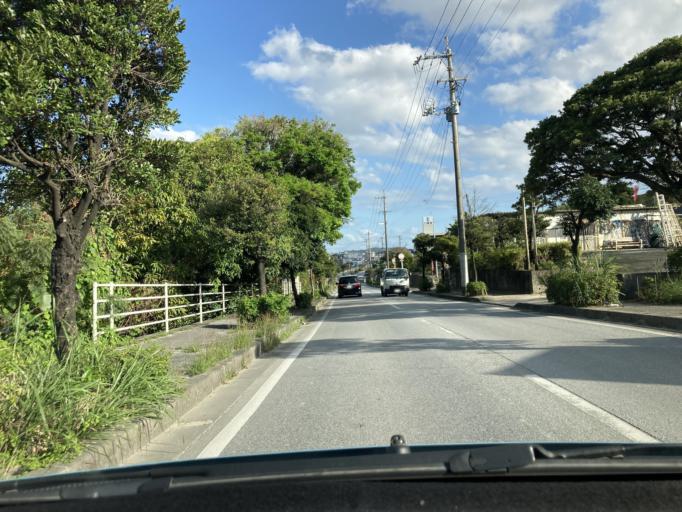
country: JP
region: Okinawa
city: Tomigusuku
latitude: 26.1901
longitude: 127.7042
